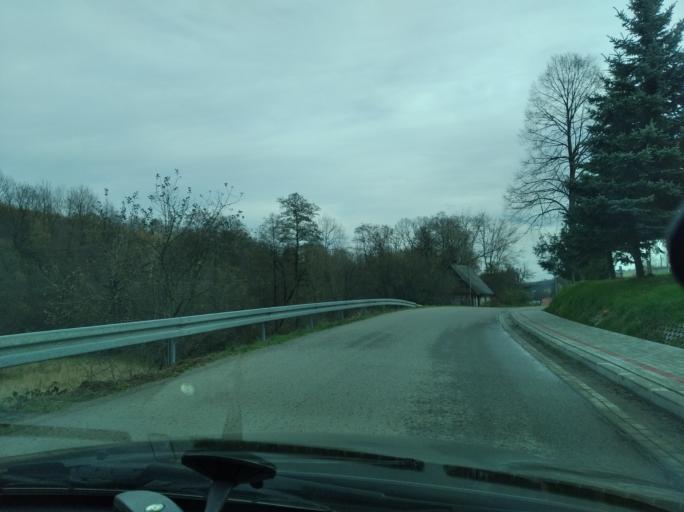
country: PL
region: Subcarpathian Voivodeship
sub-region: Powiat ropczycko-sedziszowski
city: Zagorzyce
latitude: 49.9534
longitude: 21.7229
